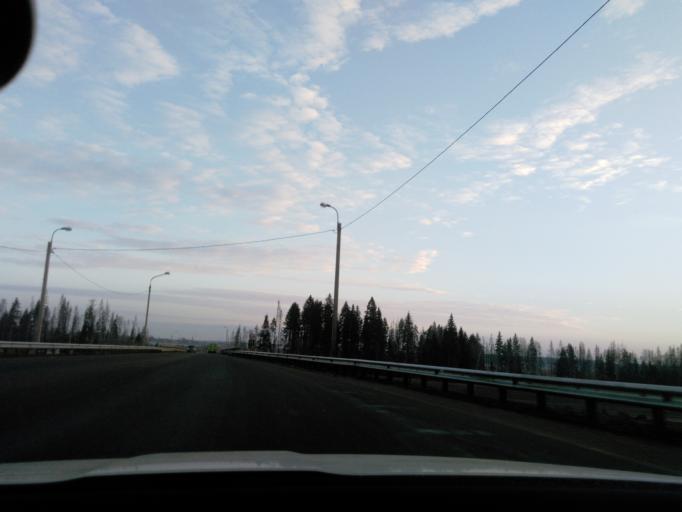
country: RU
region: Moskovskaya
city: Novopodrezkovo
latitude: 55.9706
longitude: 37.3287
